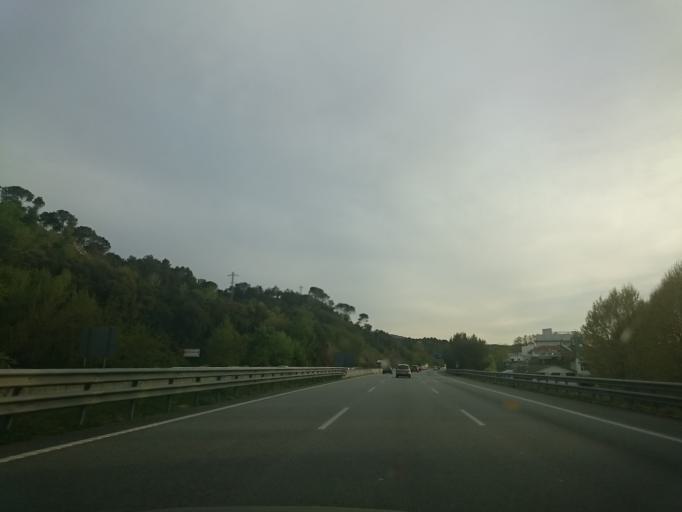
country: ES
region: Catalonia
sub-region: Provincia de Barcelona
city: Sant Celoni
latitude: 41.6783
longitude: 2.4883
